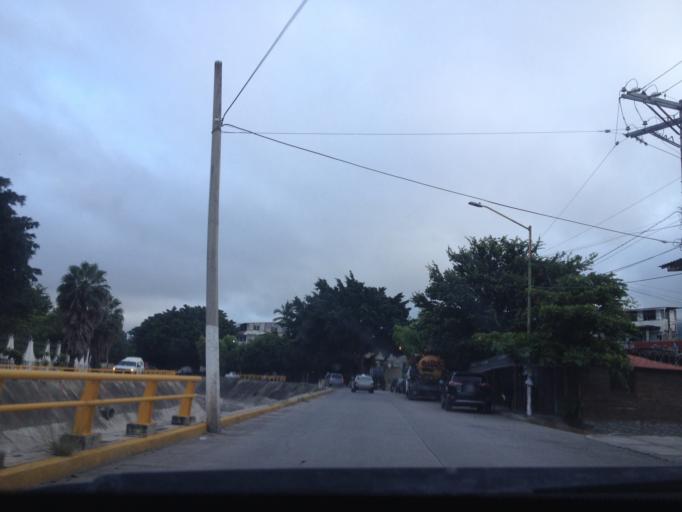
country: MX
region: Guerrero
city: Chilpancingo de los Bravos
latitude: 17.5442
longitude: -99.5018
